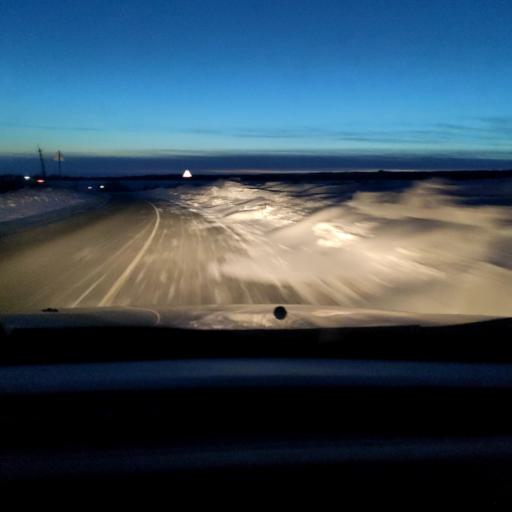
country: RU
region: Samara
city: Kinel'
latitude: 53.2842
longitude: 50.6497
